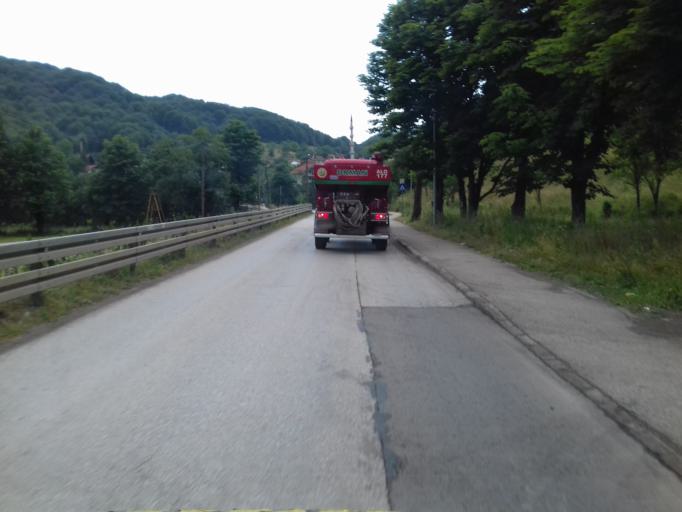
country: BA
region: Federation of Bosnia and Herzegovina
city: Visoko
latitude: 43.9652
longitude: 18.1828
